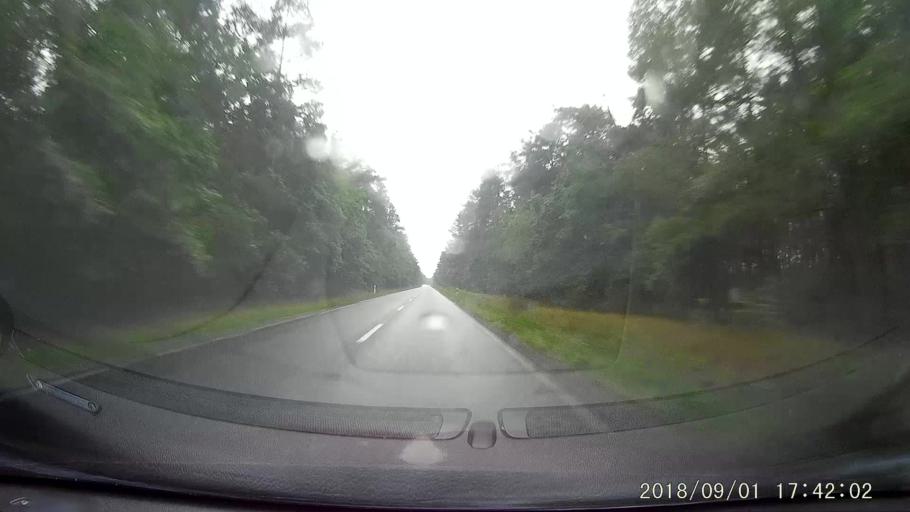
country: PL
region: Lubusz
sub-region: Powiat zaganski
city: Zagan
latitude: 51.5615
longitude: 15.2629
